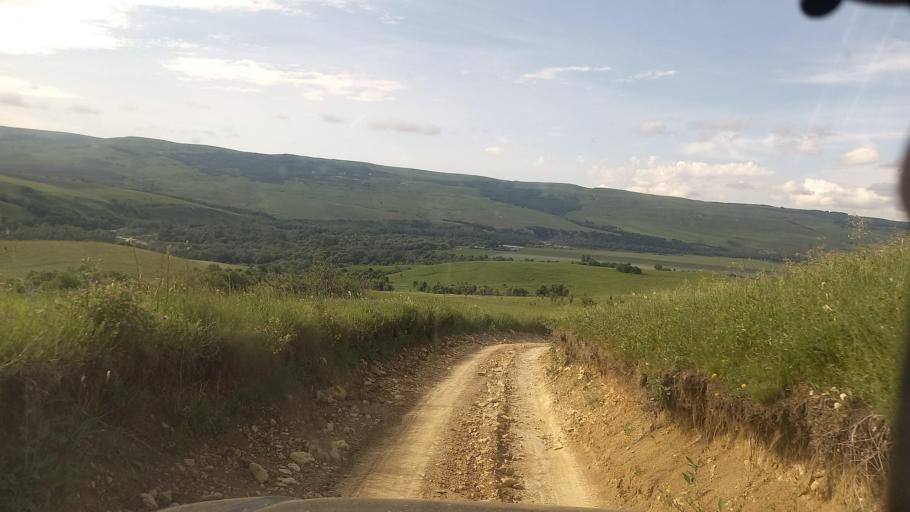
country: RU
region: Krasnodarskiy
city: Peredovaya
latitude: 44.0757
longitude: 41.3636
